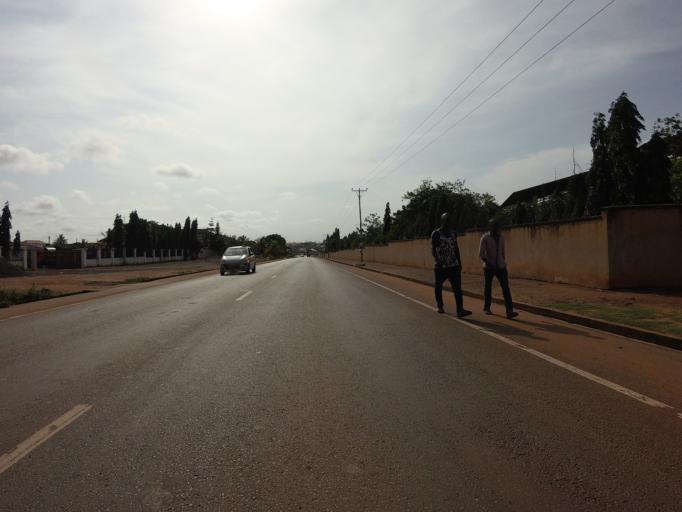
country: GH
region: Greater Accra
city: Nungua
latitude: 5.6451
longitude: -0.0978
